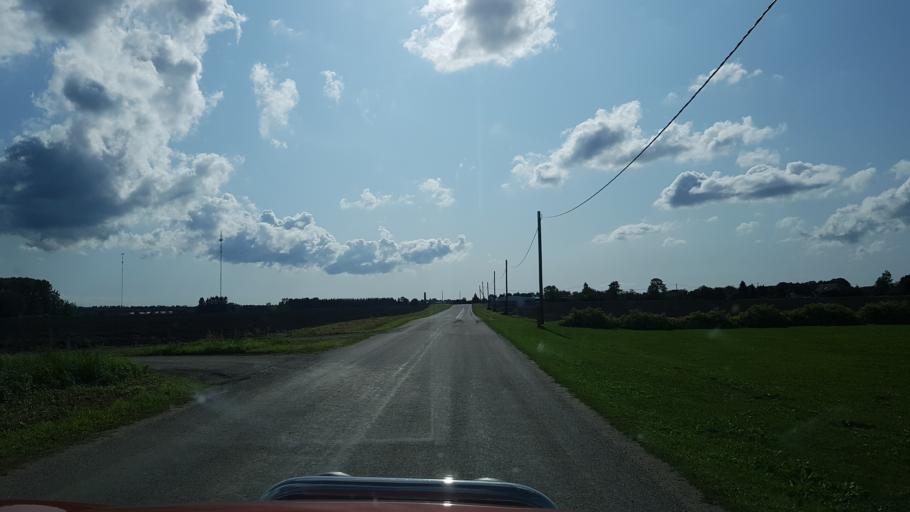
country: EE
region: Harju
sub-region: Paldiski linn
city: Paldiski
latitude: 59.2344
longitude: 24.0170
